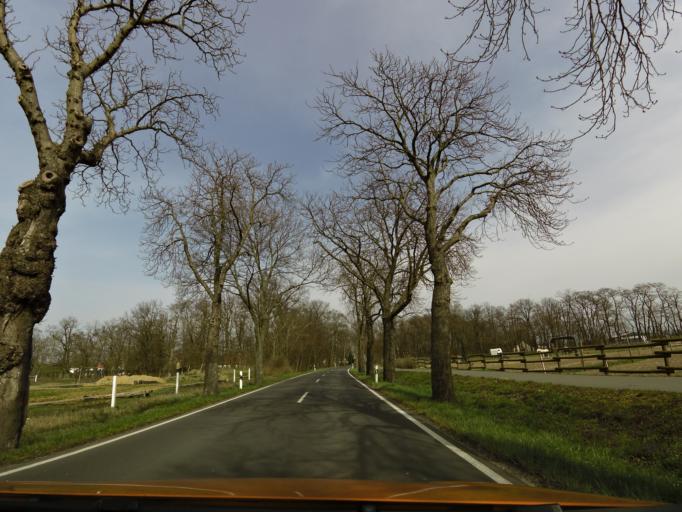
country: DE
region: Brandenburg
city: Stahnsdorf
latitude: 52.3376
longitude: 13.1877
